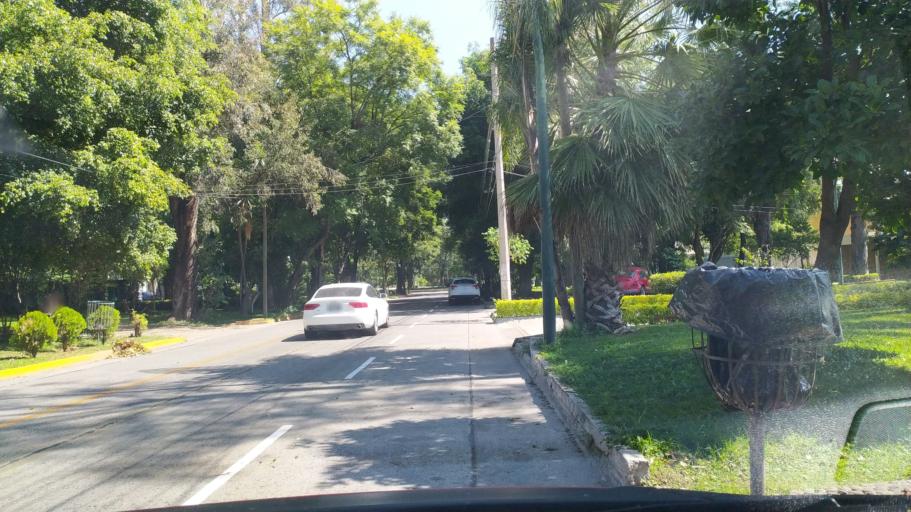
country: MX
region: Jalisco
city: Guadalajara
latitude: 20.6635
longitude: -103.4072
